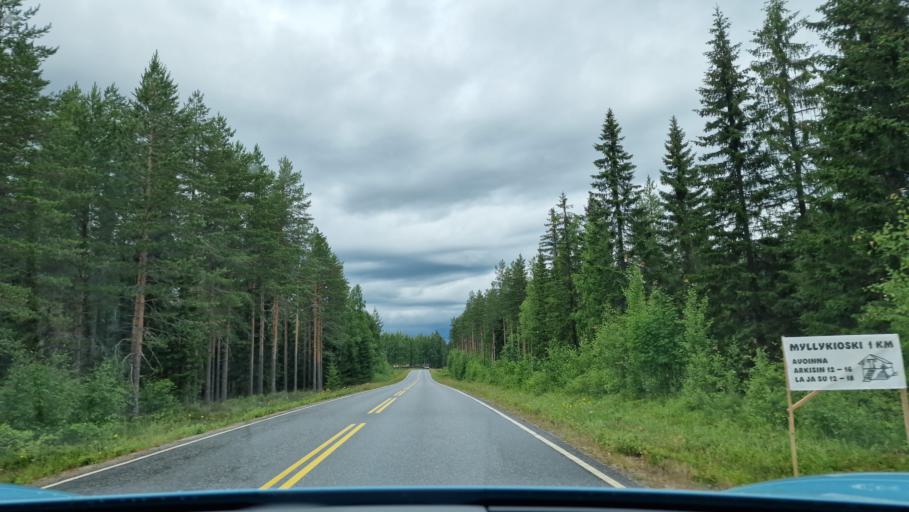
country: FI
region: Southern Ostrobothnia
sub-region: Jaerviseutu
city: Soini
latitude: 62.6906
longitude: 24.4632
